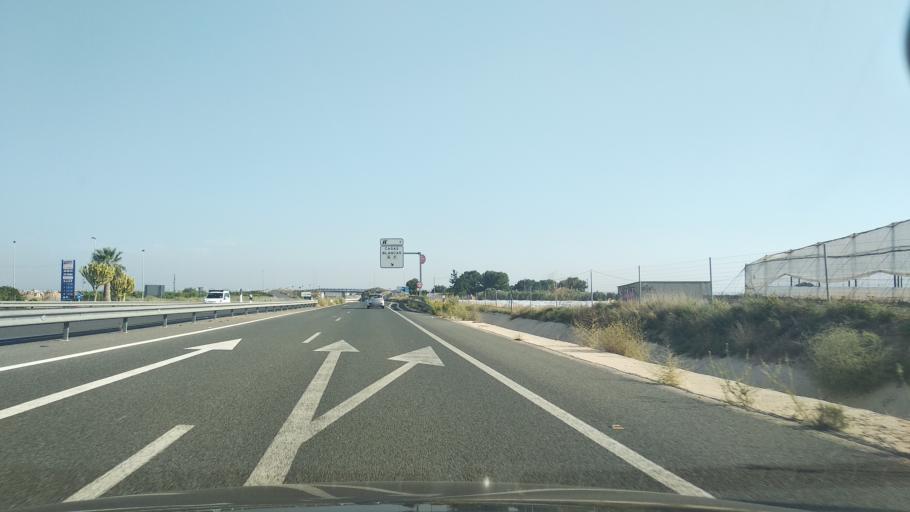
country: ES
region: Murcia
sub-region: Murcia
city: San Javier
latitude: 37.8527
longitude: -0.8809
